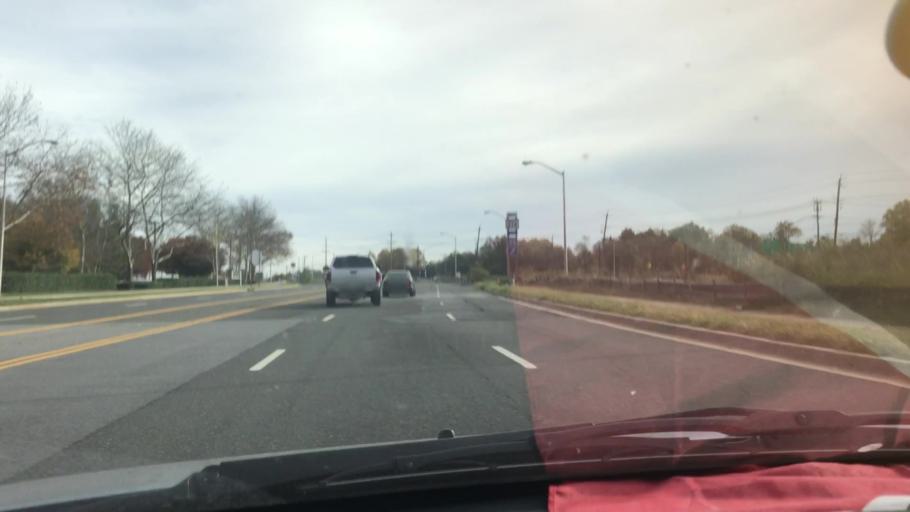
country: US
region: Maryland
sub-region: Prince George's County
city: Largo
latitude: 38.8963
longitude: -76.8386
